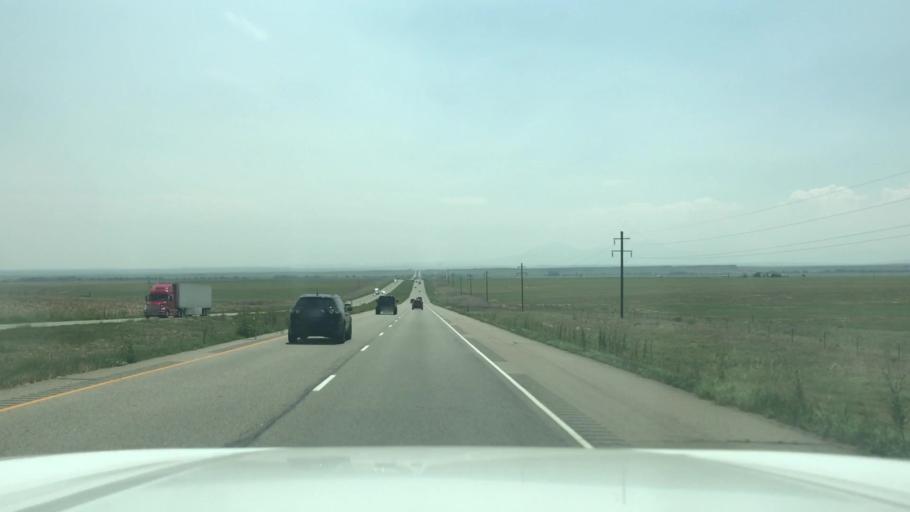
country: US
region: Colorado
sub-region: Pueblo County
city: Colorado City
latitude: 37.8852
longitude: -104.8294
